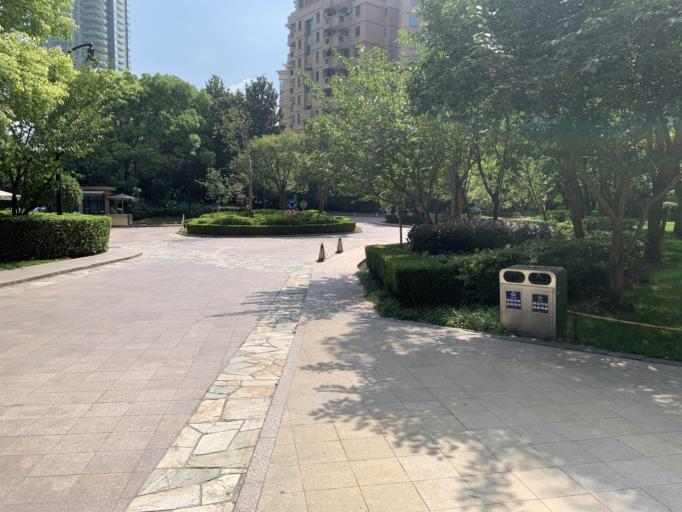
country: CN
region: Shanghai Shi
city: Pudong
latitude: 31.2309
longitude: 121.5049
